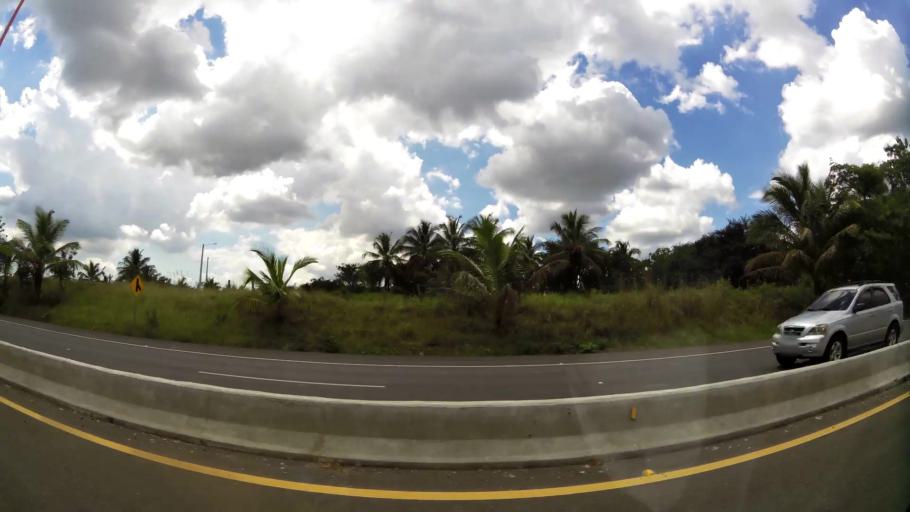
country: DO
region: Nacional
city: Santo Domingo
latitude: 18.5692
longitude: -69.9804
